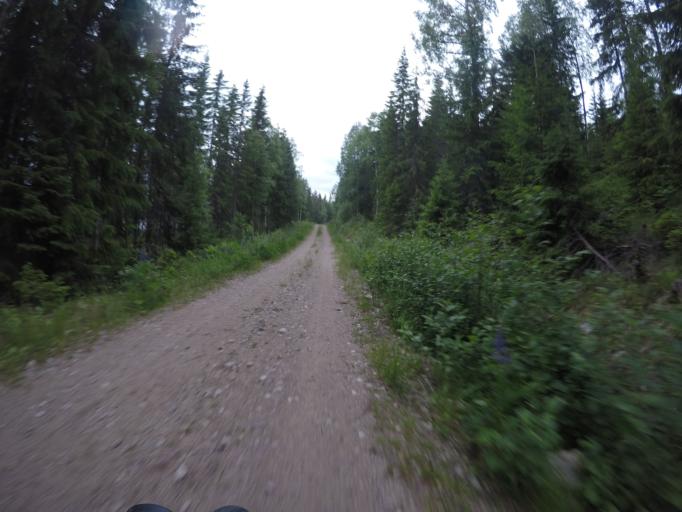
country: SE
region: Dalarna
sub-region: Ludvika Kommun
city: Abborrberget
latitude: 60.0396
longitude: 14.5944
